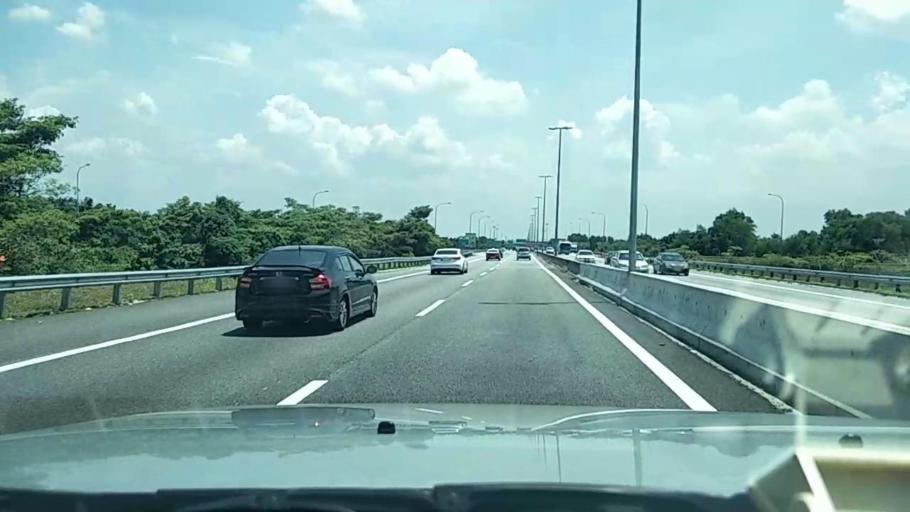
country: MY
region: Putrajaya
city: Putrajaya
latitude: 2.9282
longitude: 101.6218
